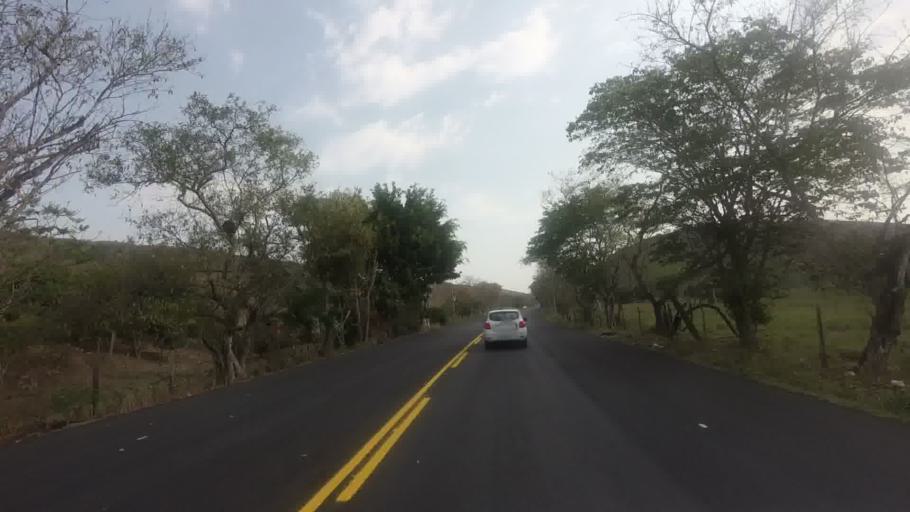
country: BR
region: Rio de Janeiro
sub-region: Bom Jesus Do Itabapoana
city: Bom Jesus do Itabapoana
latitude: -21.2265
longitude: -41.7437
